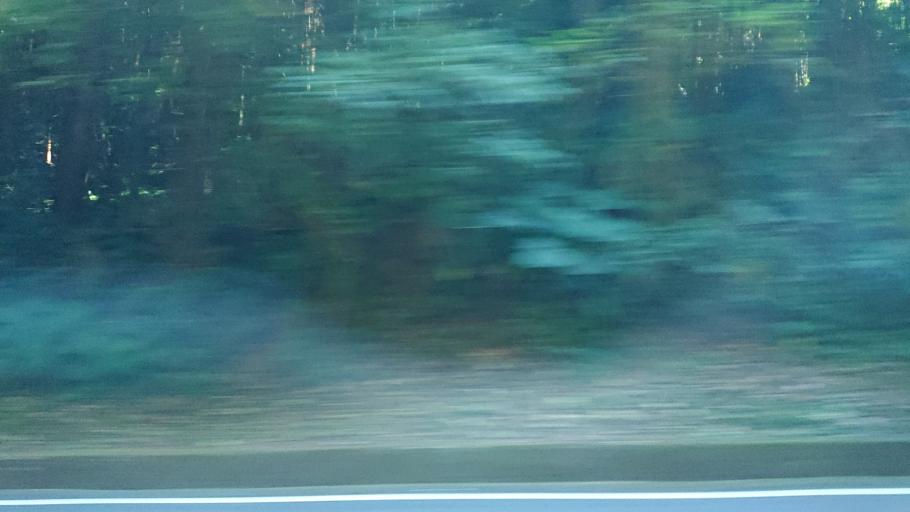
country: TW
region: Taiwan
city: Lugu
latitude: 23.4890
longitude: 120.7584
